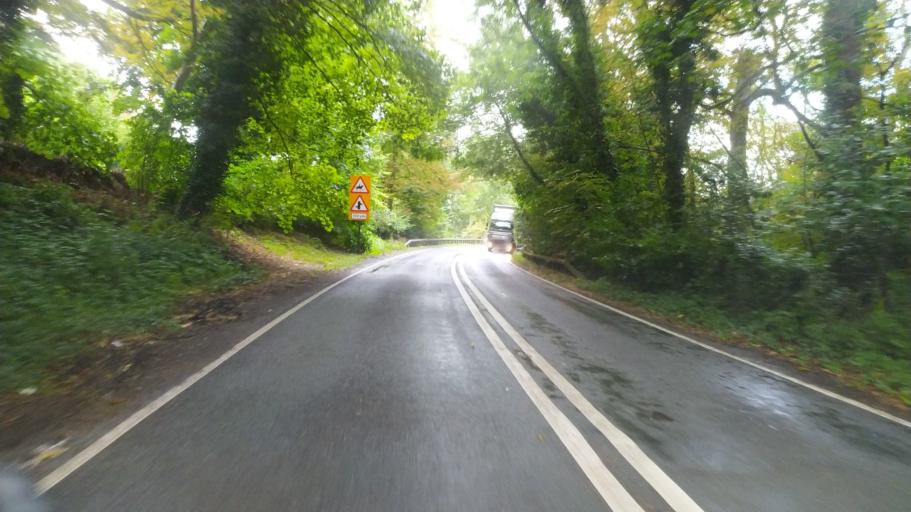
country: GB
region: England
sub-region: Hampshire
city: Swanmore
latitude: 51.0049
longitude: -1.1094
